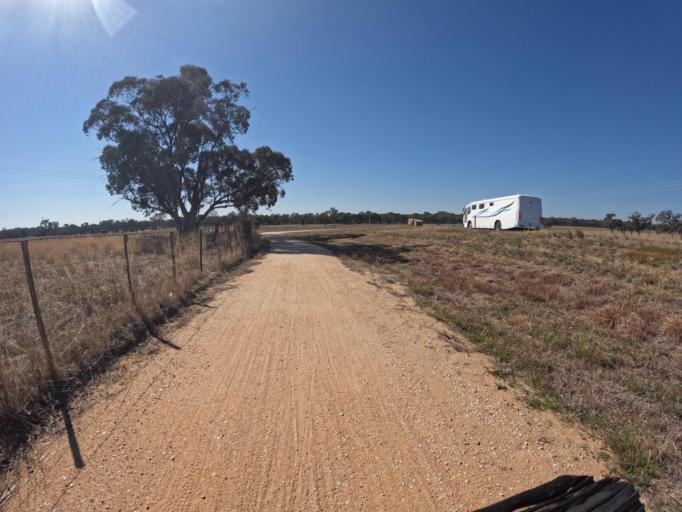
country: AU
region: Victoria
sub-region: Greater Bendigo
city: Epsom
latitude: -36.7872
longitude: 144.5216
